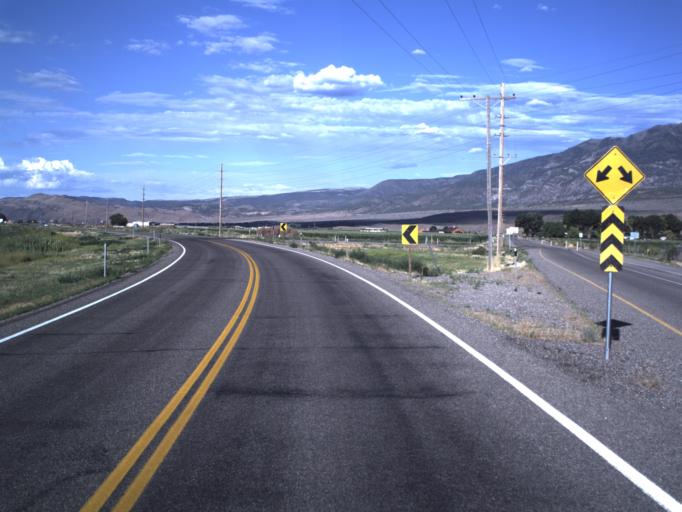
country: US
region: Utah
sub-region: Sevier County
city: Monroe
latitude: 38.6833
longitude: -112.1328
